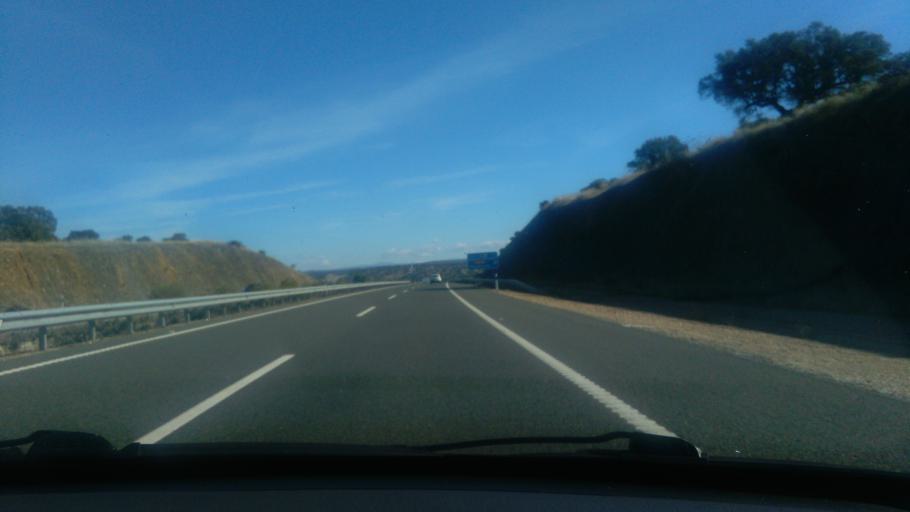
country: ES
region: Extremadura
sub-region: Provincia de Caceres
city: Plasenzuela
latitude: 39.4403
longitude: -6.0723
